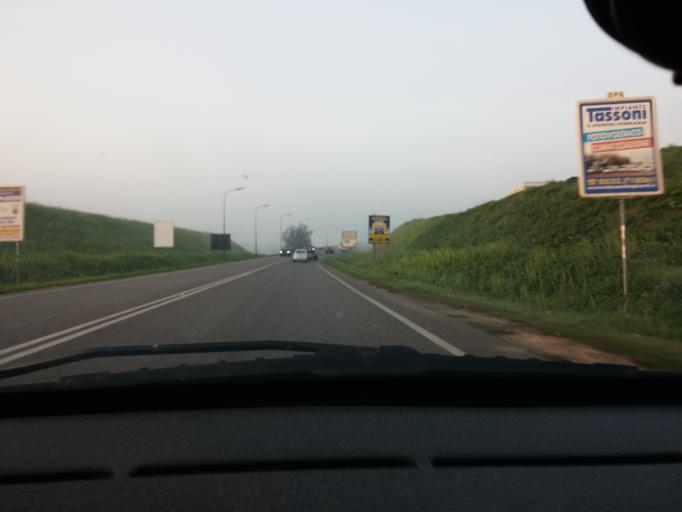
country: IT
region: Emilia-Romagna
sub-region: Provincia di Ferrara
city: Ferrara
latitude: 44.8335
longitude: 11.6005
